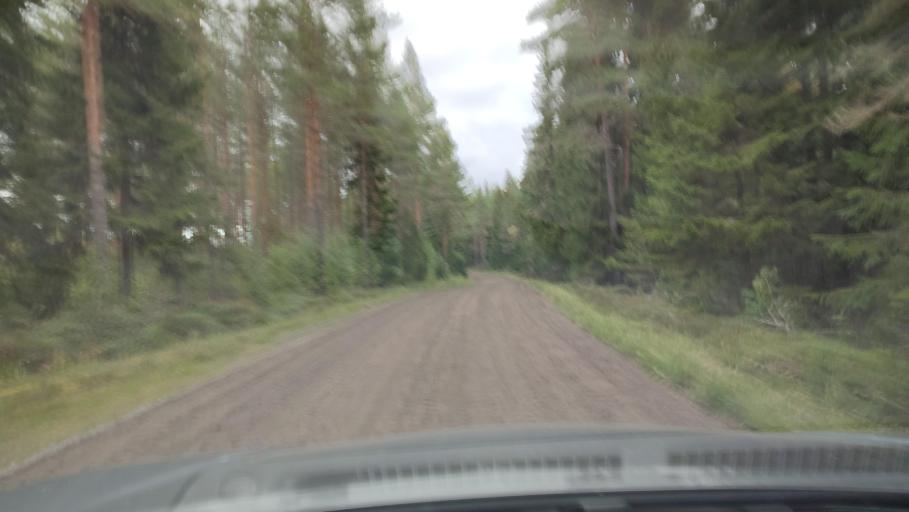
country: FI
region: Southern Ostrobothnia
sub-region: Suupohja
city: Karijoki
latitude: 62.2295
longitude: 21.5730
